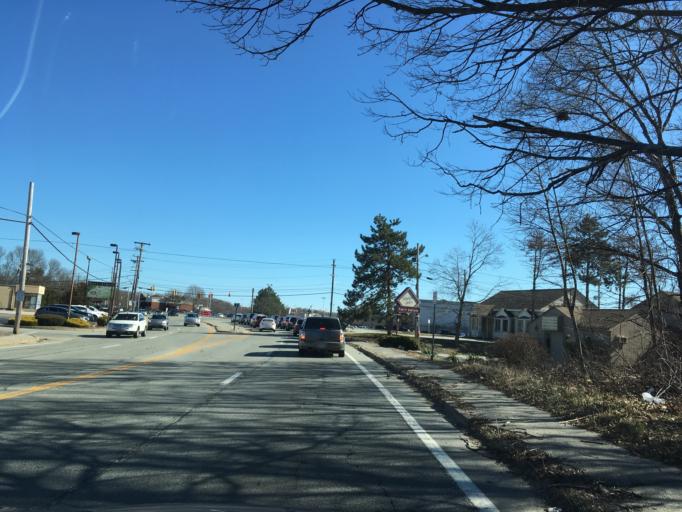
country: US
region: Rhode Island
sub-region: Kent County
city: West Warwick
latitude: 41.7286
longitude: -71.4767
